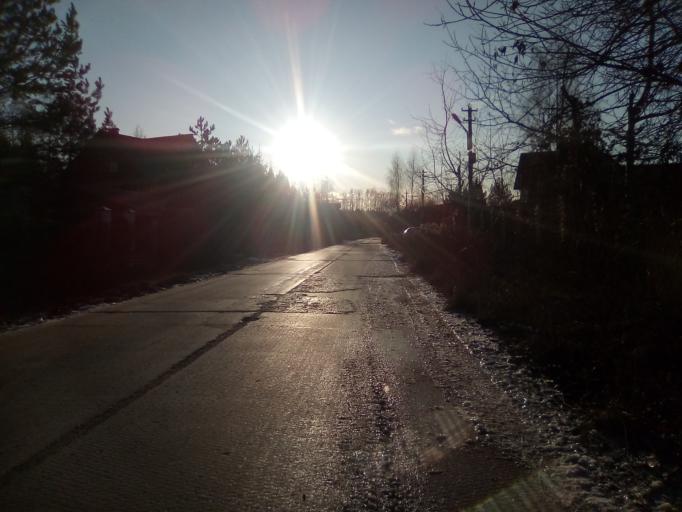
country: RU
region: Moskovskaya
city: Zhavoronki
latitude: 55.6447
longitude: 37.1485
